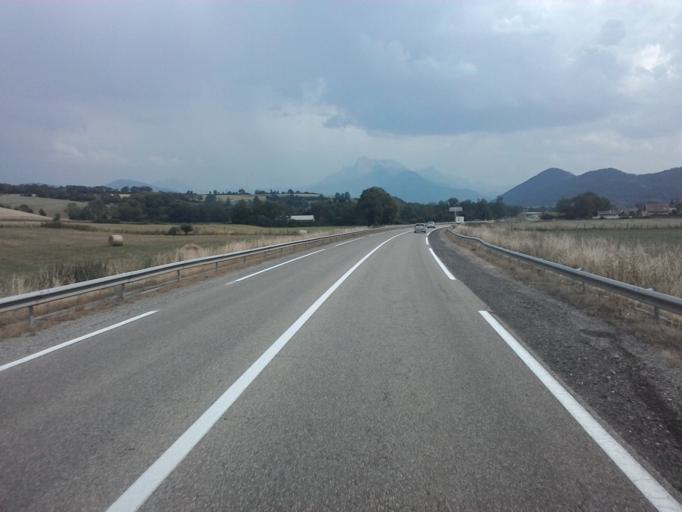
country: FR
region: Rhone-Alpes
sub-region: Departement de l'Isere
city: Pierre-Chatel
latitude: 44.9582
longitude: 5.7810
